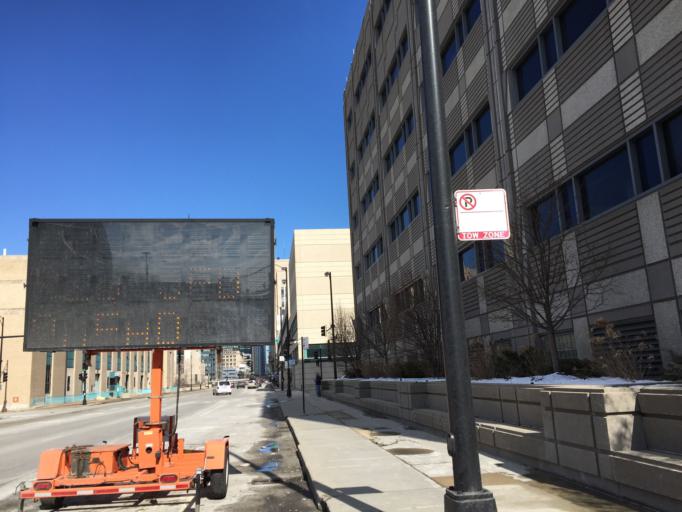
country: US
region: Illinois
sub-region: Cook County
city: Chicago
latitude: 41.8715
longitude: -87.6393
